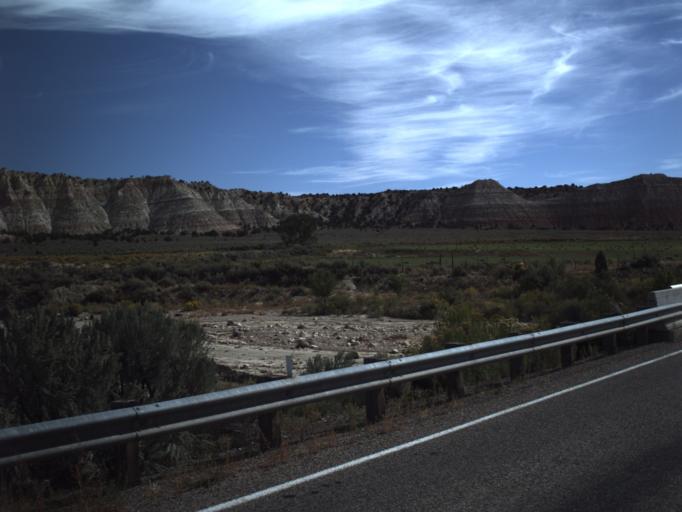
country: US
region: Utah
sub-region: Garfield County
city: Panguitch
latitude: 37.5678
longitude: -112.0520
